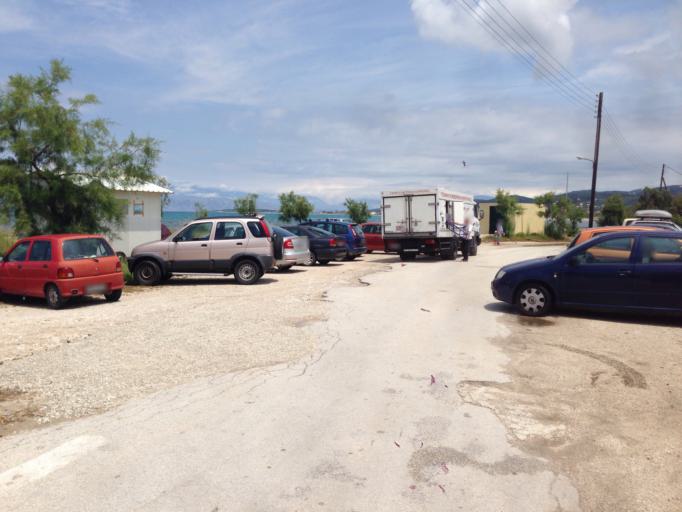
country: GR
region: Ionian Islands
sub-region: Nomos Kerkyras
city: Acharavi
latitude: 39.7905
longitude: 19.7909
